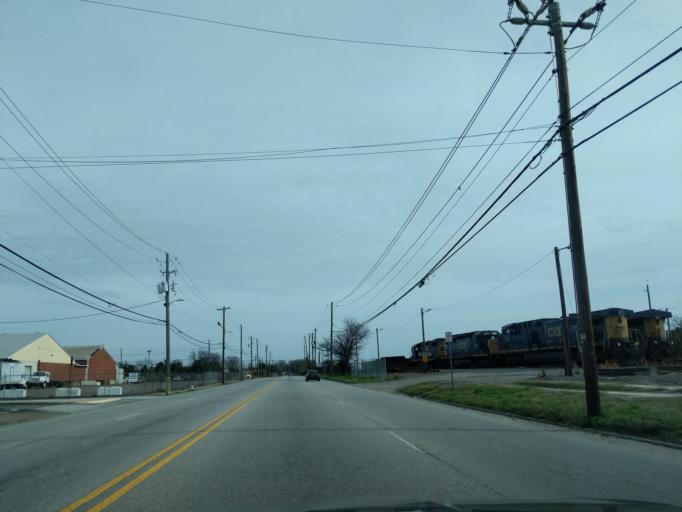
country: US
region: Georgia
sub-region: Richmond County
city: Augusta
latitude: 33.4602
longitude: -81.9642
